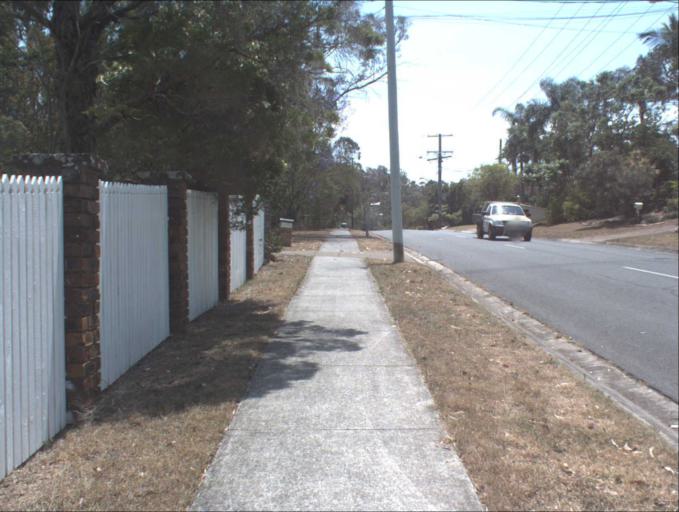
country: AU
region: Queensland
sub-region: Logan
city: Beenleigh
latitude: -27.6684
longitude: 153.1937
